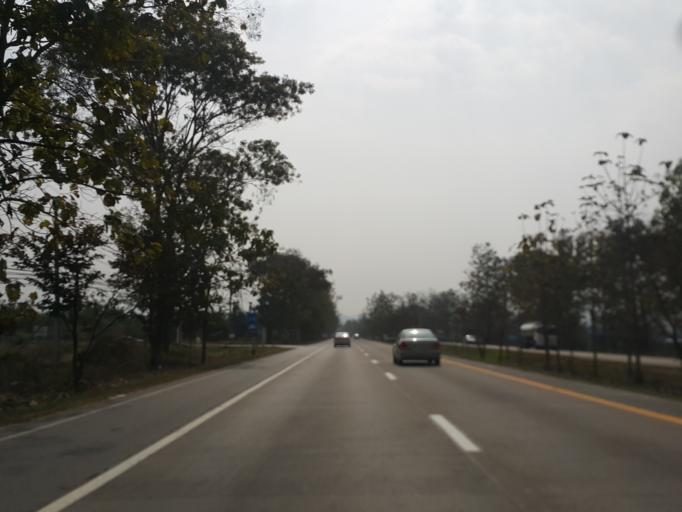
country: TH
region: Lamphun
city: Lamphun
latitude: 18.5310
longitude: 99.0789
